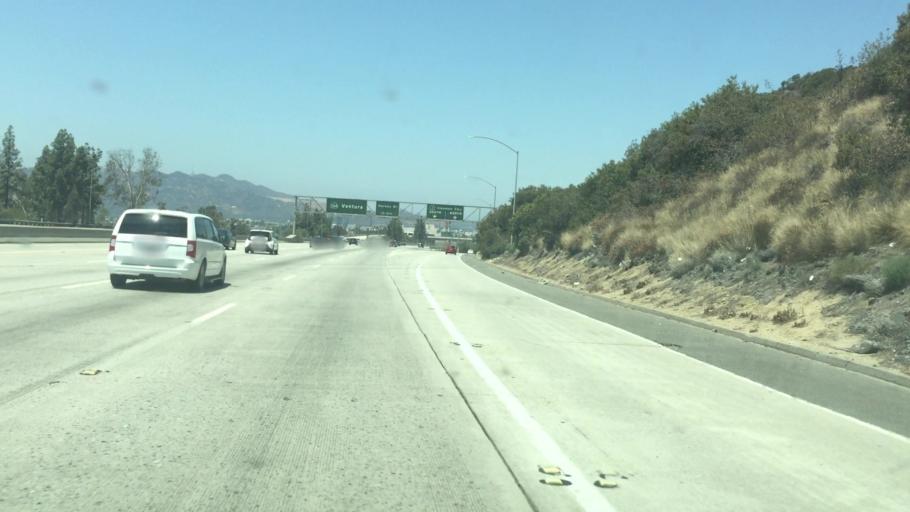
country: US
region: California
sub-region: Los Angeles County
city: Glendale
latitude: 34.1452
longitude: -118.2170
